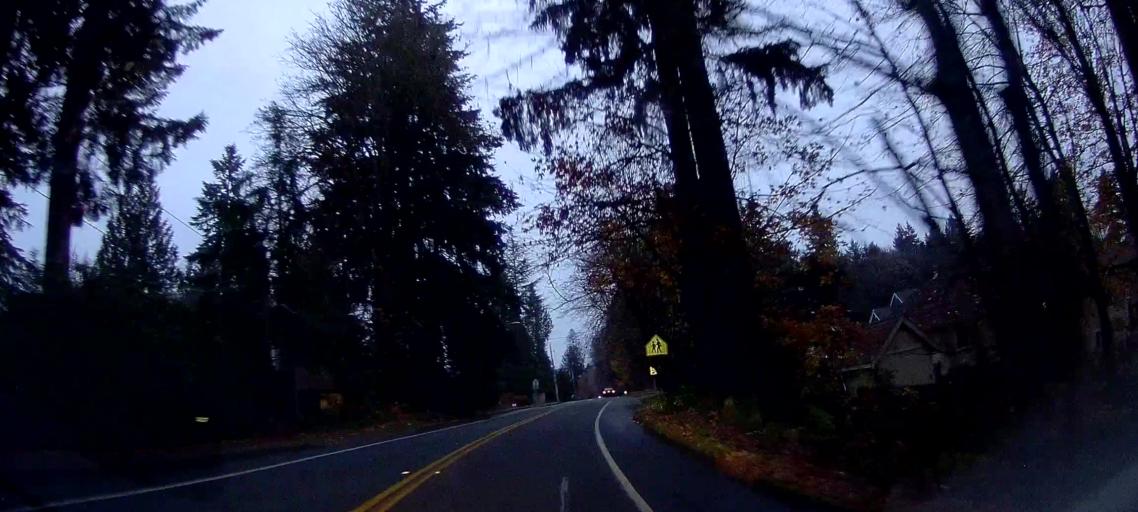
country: US
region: Washington
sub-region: Thurston County
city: Olympia
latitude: 47.0257
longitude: -122.8737
